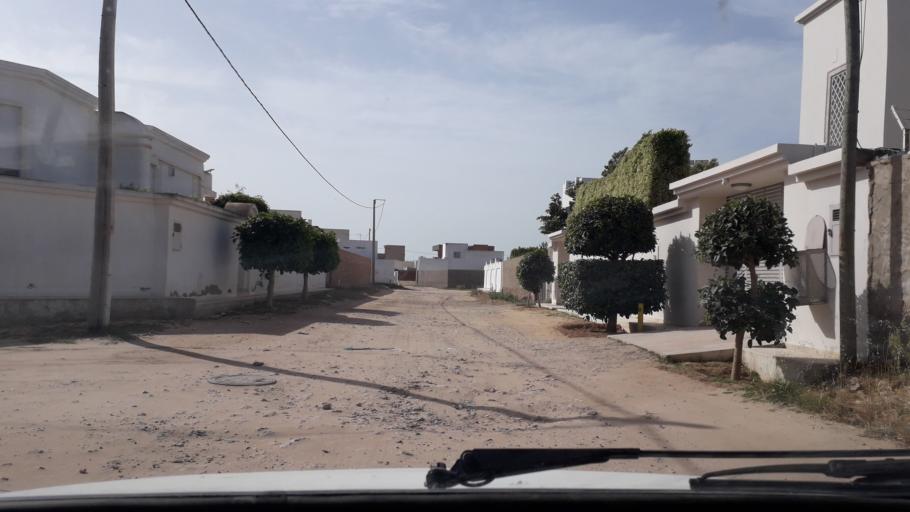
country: TN
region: Safaqis
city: Al Qarmadah
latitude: 34.8088
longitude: 10.7703
